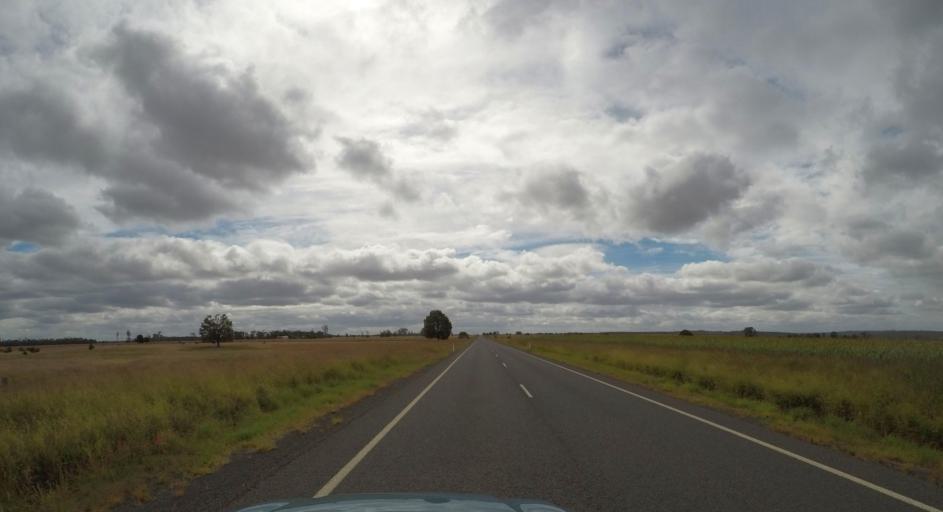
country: AU
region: Queensland
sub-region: South Burnett
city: Kingaroy
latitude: -26.3786
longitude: 151.2463
